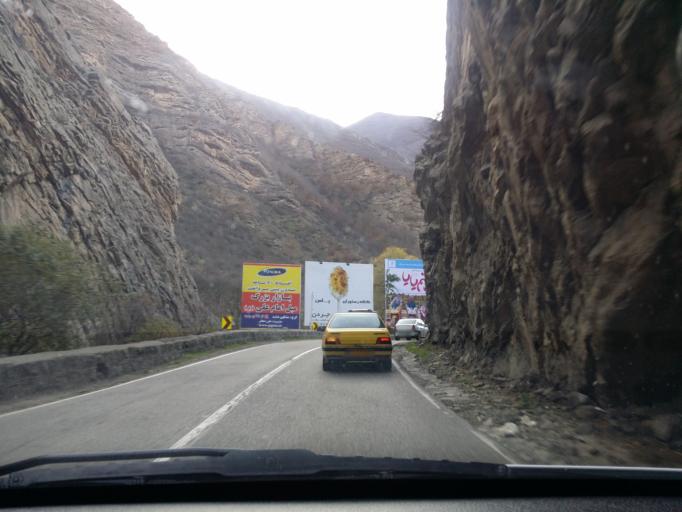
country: IR
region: Mazandaran
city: Chalus
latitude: 36.3160
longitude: 51.2475
